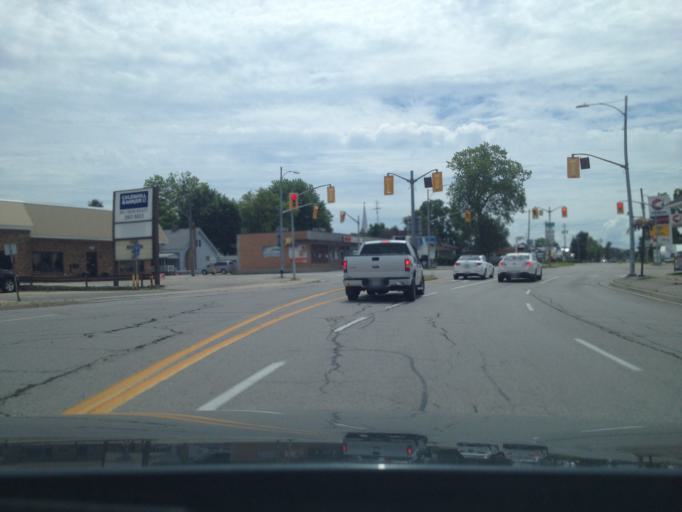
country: CA
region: Ontario
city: Norfolk County
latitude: 42.8543
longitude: -80.4942
